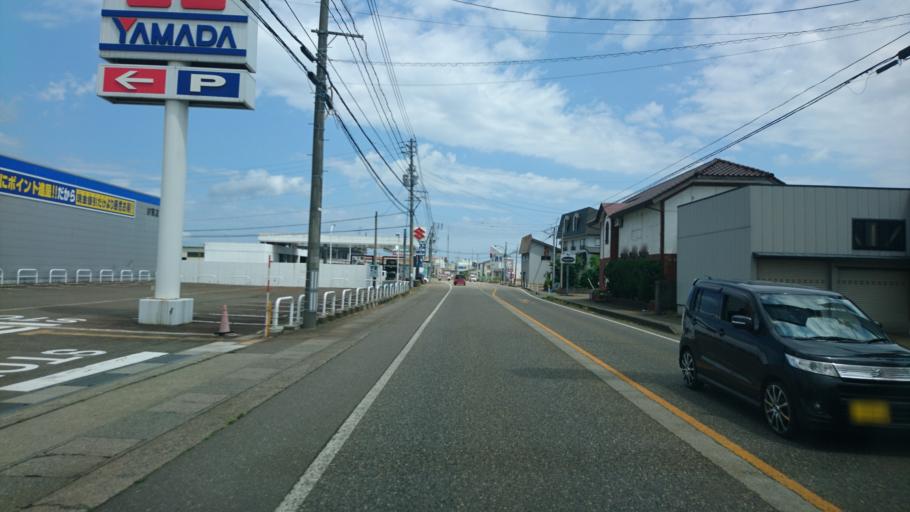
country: JP
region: Niigata
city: Arai
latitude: 37.0548
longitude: 138.2605
